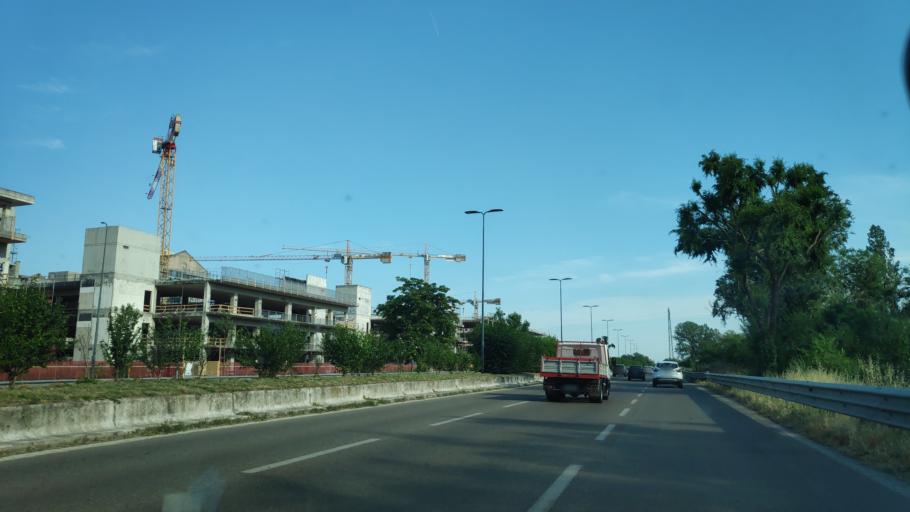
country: IT
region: Lombardy
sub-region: Citta metropolitana di Milano
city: Noverasco-Sporting Mirasole
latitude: 45.4265
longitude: 9.1964
